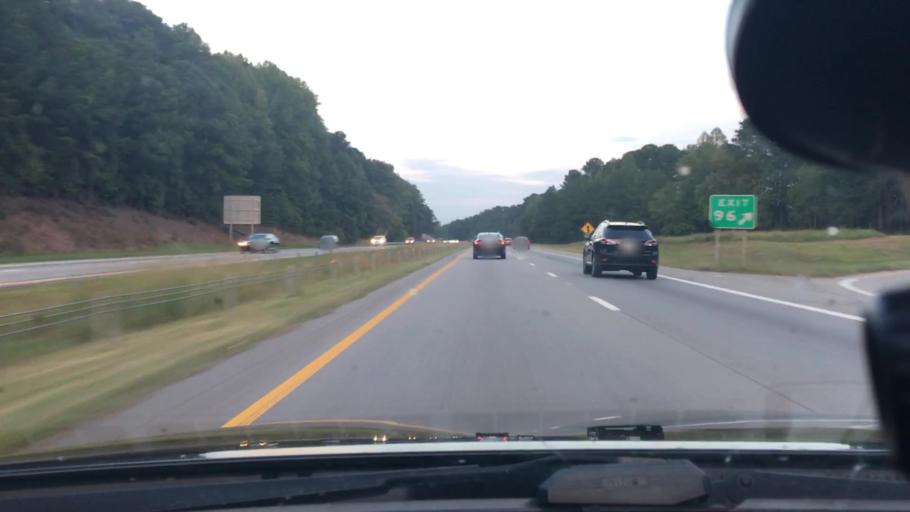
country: US
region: North Carolina
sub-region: Wake County
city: Apex
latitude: 35.7241
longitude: -78.8213
